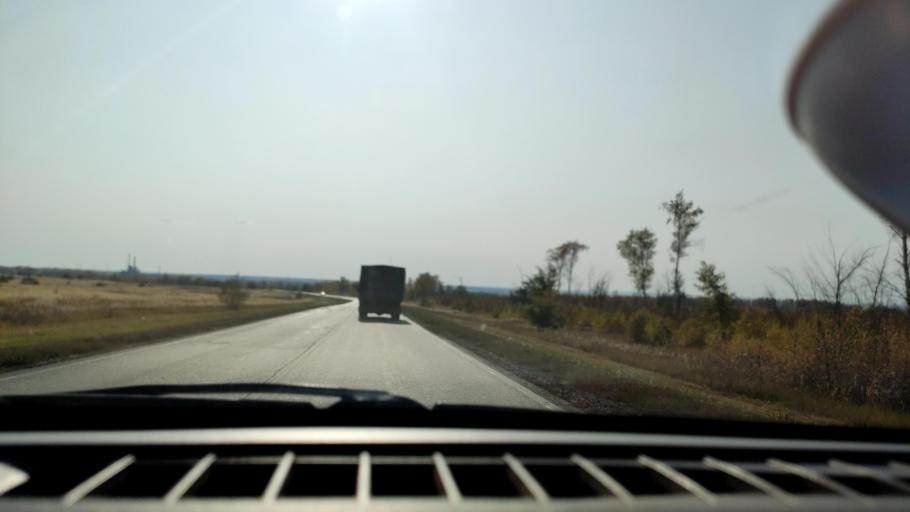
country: RU
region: Samara
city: Smyshlyayevka
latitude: 53.1104
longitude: 50.3544
